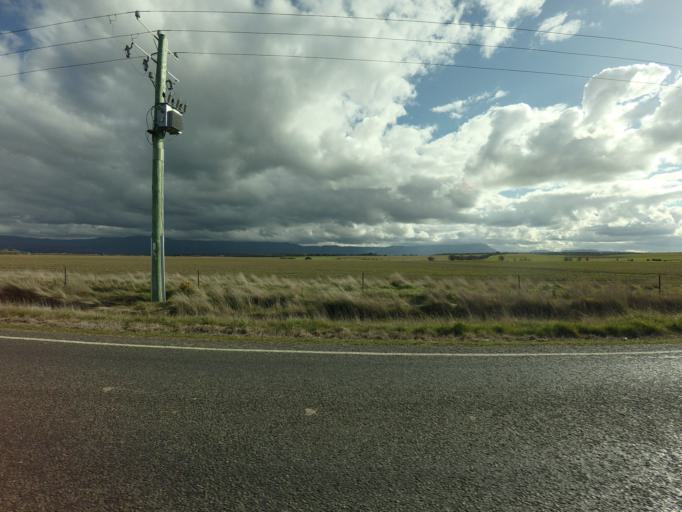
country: AU
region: Tasmania
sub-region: Northern Midlands
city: Longford
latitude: -41.7063
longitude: 147.0789
